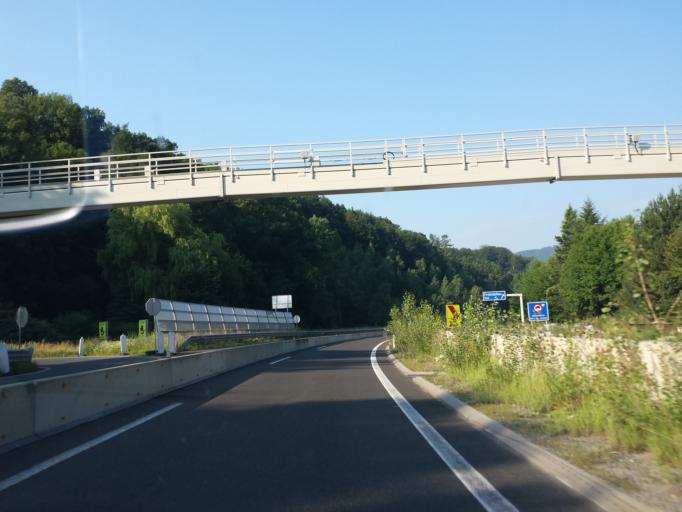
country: AT
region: Styria
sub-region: Politischer Bezirk Graz-Umgebung
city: Frohnleiten
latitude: 47.2671
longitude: 15.3299
